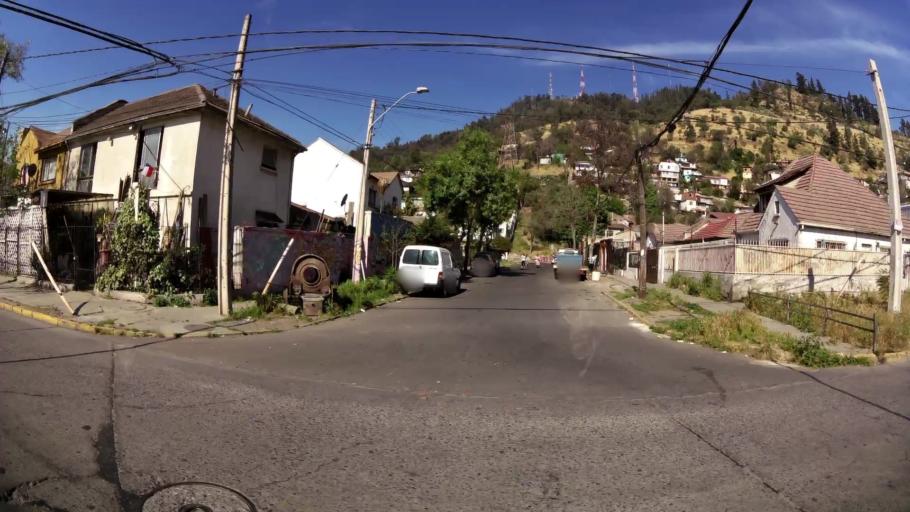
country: CL
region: Santiago Metropolitan
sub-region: Provincia de Santiago
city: Santiago
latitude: -33.4166
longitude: -70.6386
